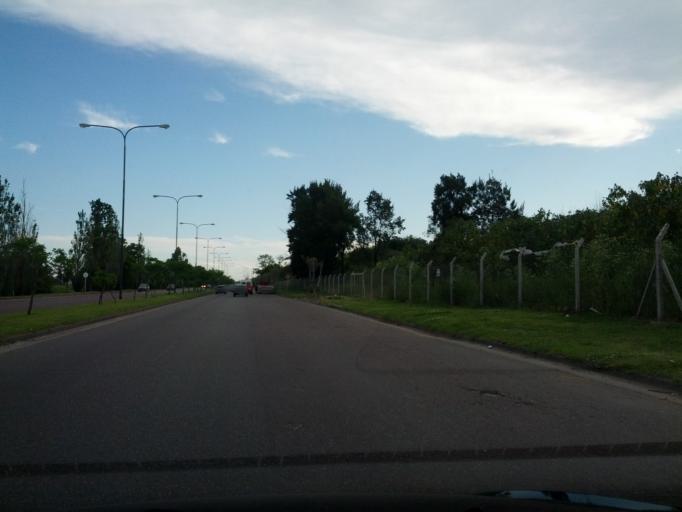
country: AR
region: Buenos Aires F.D.
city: Villa Lugano
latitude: -34.6753
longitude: -58.4366
